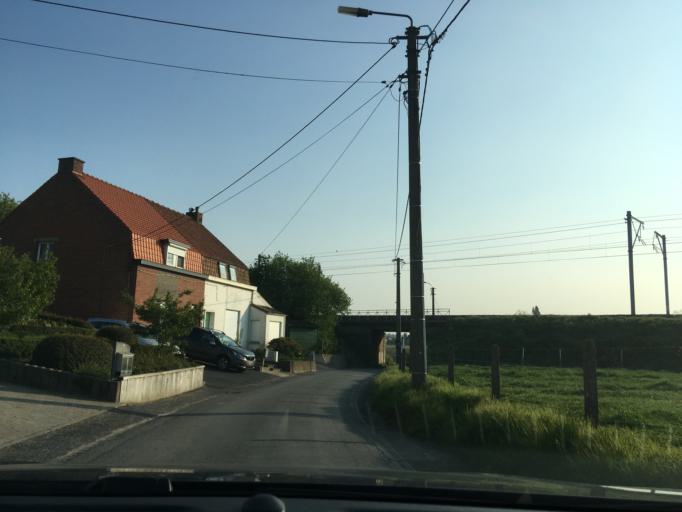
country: BE
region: Flanders
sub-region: Provincie West-Vlaanderen
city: Lichtervelde
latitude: 51.0140
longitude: 3.1401
